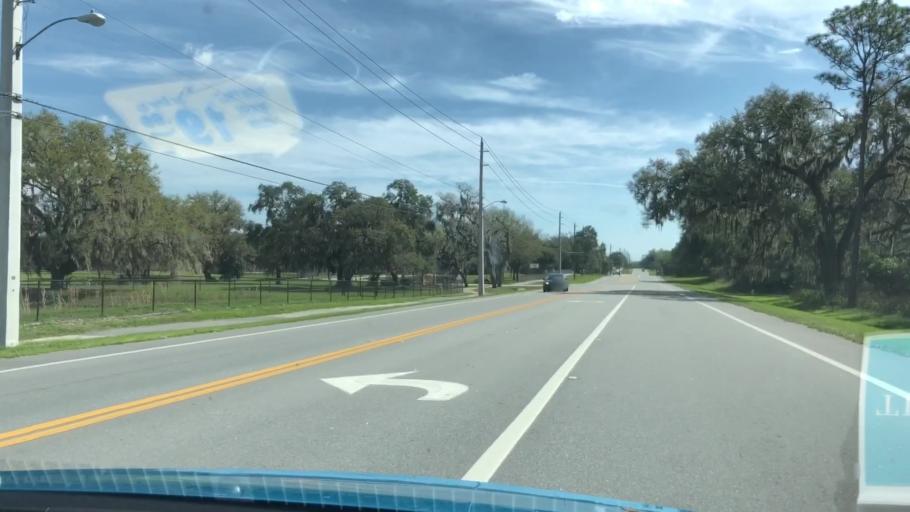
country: US
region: Florida
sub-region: Seminole County
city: Midway
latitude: 28.8538
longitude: -81.1776
